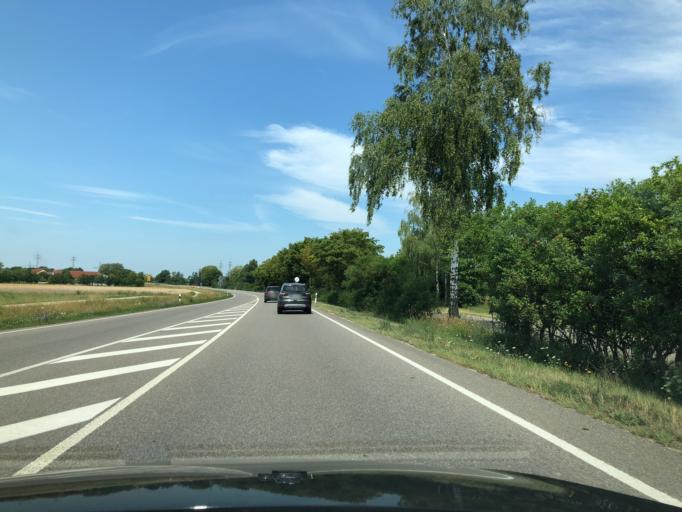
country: DE
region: Bavaria
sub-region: Upper Bavaria
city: Manching
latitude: 48.7163
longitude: 11.4613
